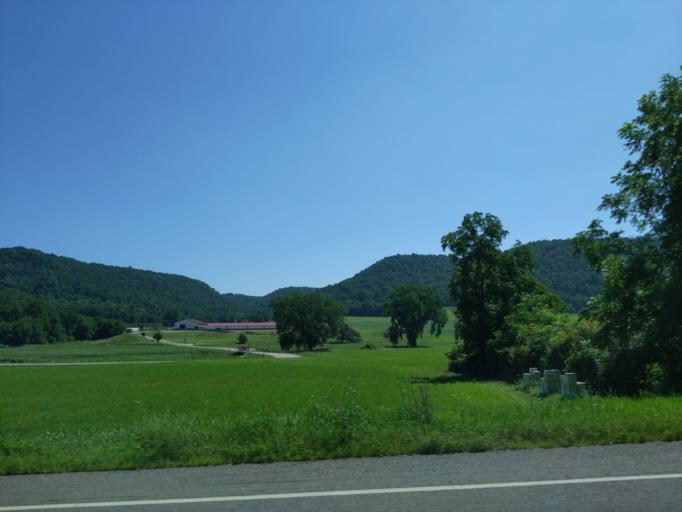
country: US
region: Wisconsin
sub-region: Vernon County
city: Westby
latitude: 43.6828
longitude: -91.0445
